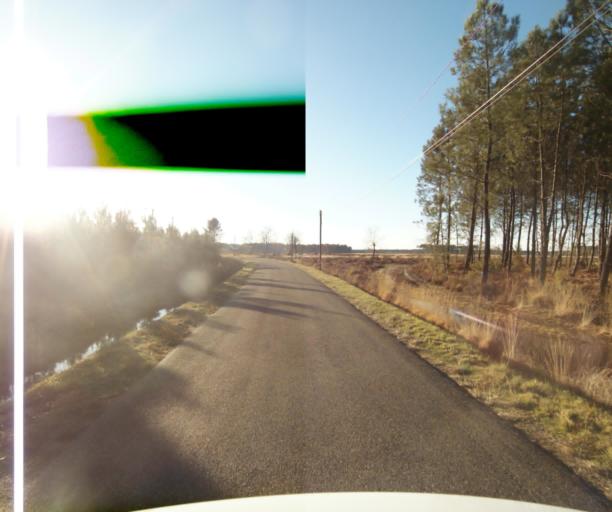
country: FR
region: Aquitaine
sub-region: Departement des Landes
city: Gabarret
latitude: 44.1093
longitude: -0.1157
